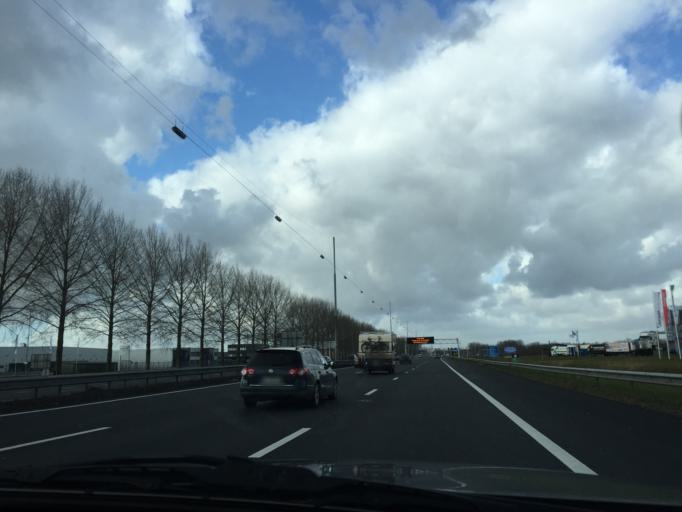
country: NL
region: Gelderland
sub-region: Gemeente Duiven
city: Duiven
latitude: 51.9642
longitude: 6.0110
